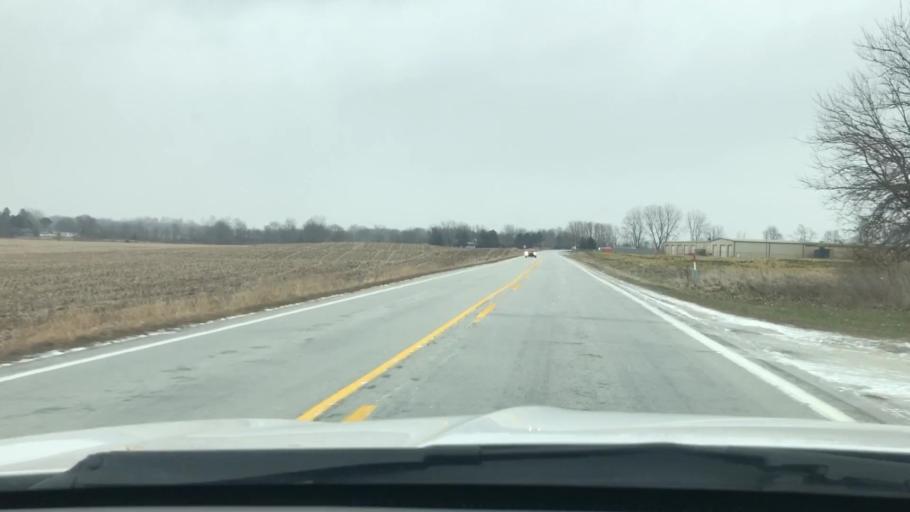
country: US
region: Indiana
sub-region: Fulton County
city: Akron
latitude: 41.0398
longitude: -86.0838
